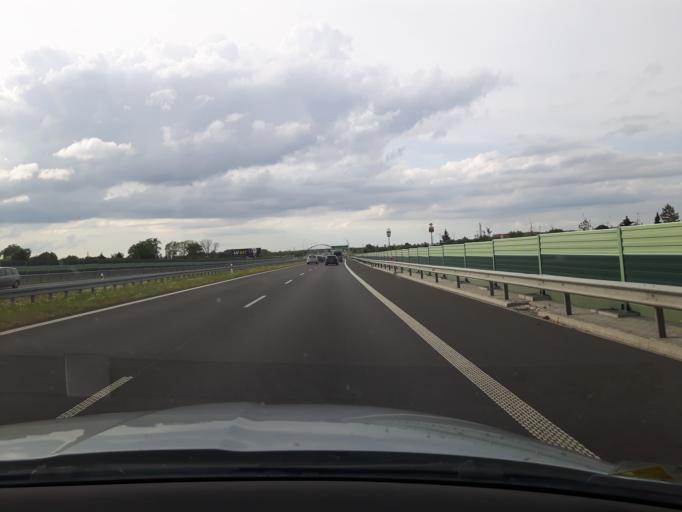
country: PL
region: Pomeranian Voivodeship
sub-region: Powiat nowodworski
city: Nowy Dwor Gdanski
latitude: 54.2050
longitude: 19.1100
